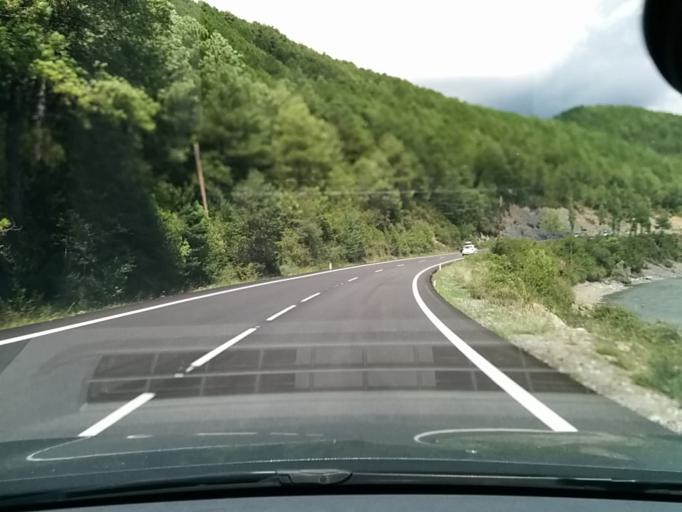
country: ES
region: Aragon
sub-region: Provincia de Huesca
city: Laspuna
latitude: 42.5186
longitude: 0.1402
